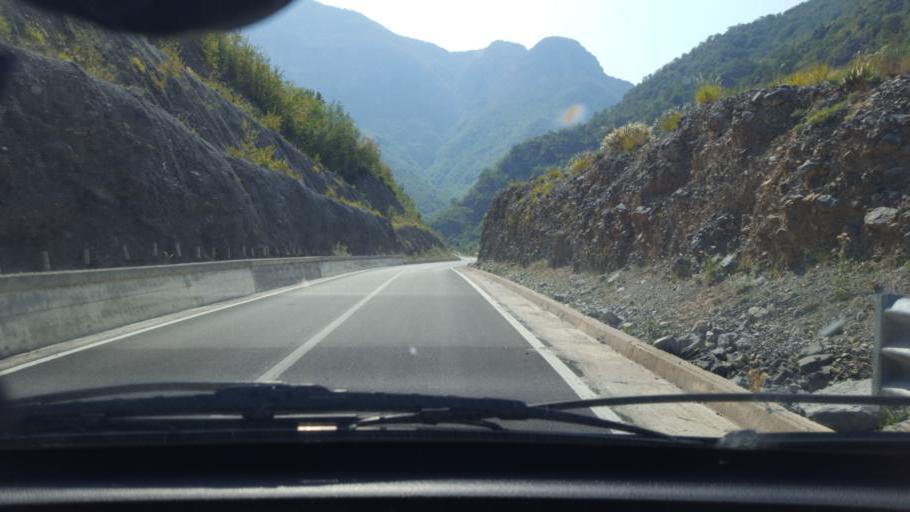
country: AL
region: Shkoder
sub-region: Rrethi i Malesia e Madhe
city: Kastrat
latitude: 42.4347
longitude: 19.5362
